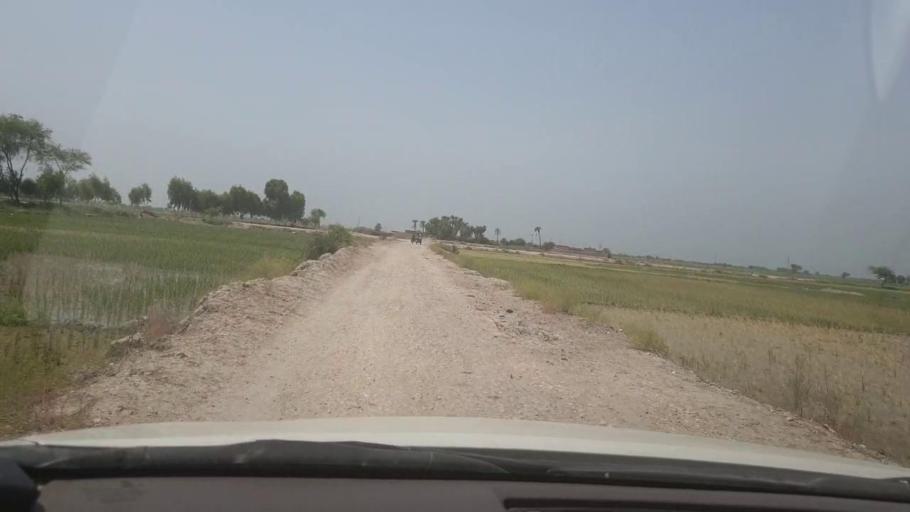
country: PK
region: Sindh
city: Shikarpur
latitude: 27.9595
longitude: 68.5925
